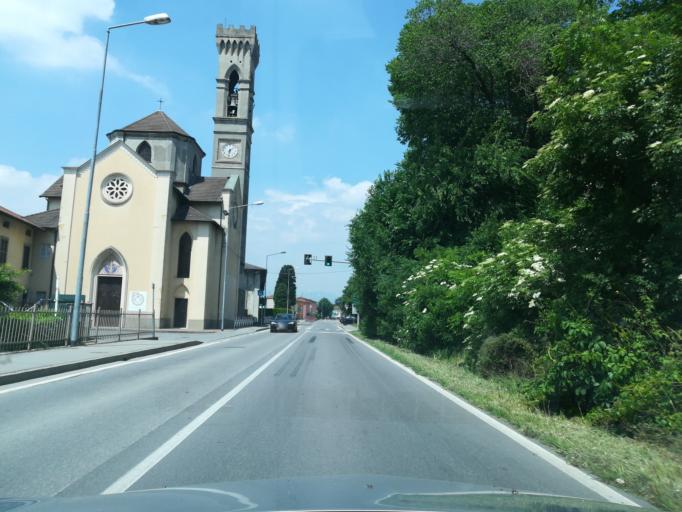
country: IT
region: Lombardy
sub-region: Provincia di Bergamo
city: Grassobbio
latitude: 45.6501
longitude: 9.7478
